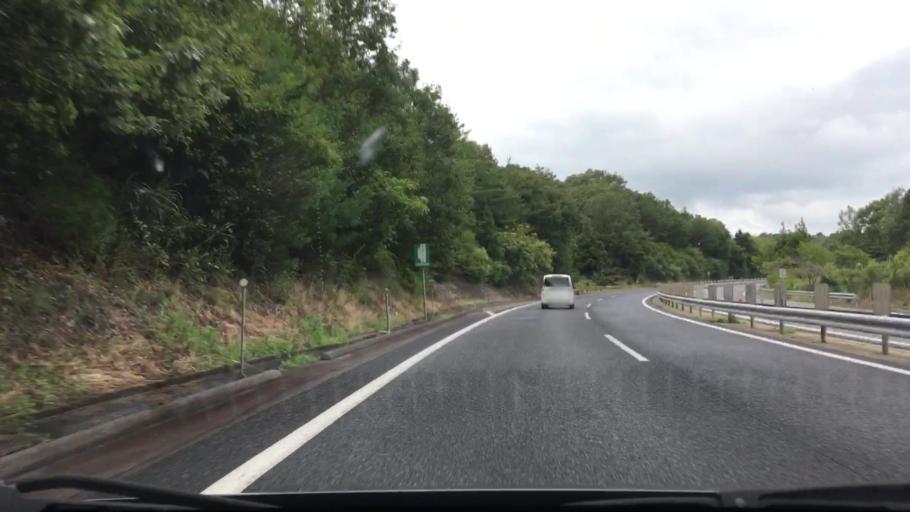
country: JP
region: Hiroshima
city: Miyoshi
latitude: 34.7435
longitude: 132.7216
